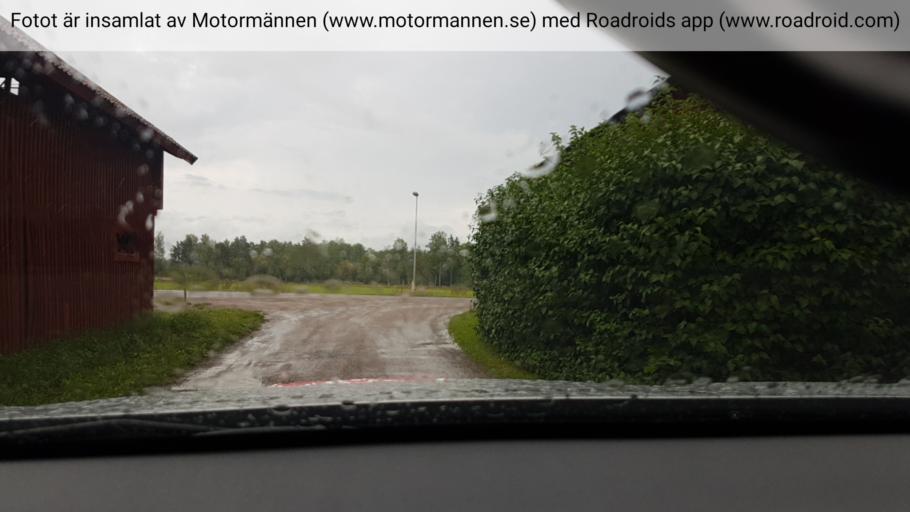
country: SE
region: Uppsala
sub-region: Tierps Kommun
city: Karlholmsbruk
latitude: 60.5117
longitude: 17.5982
